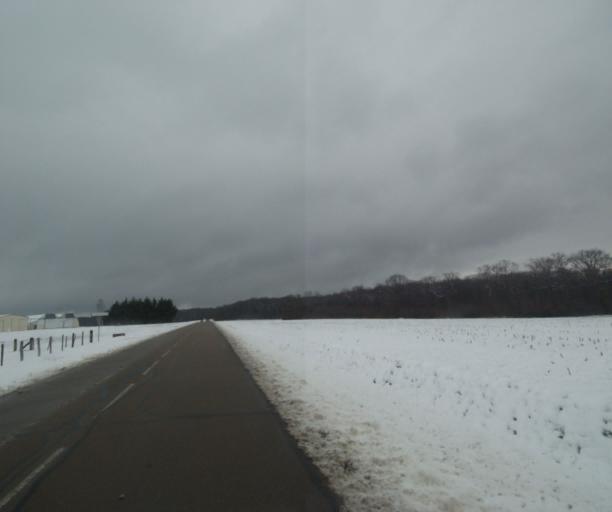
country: FR
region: Champagne-Ardenne
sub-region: Departement de la Haute-Marne
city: Laneuville-a-Remy
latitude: 48.4335
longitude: 4.8549
